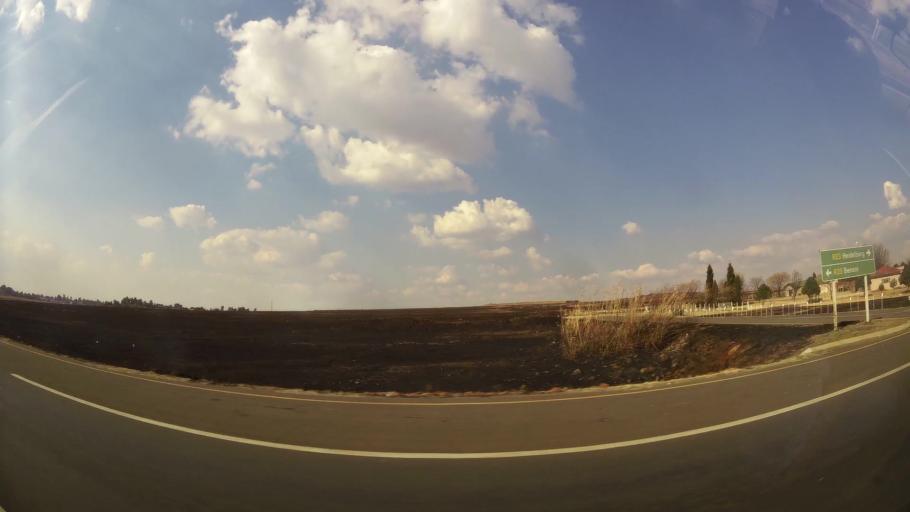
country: ZA
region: Gauteng
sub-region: Ekurhuleni Metropolitan Municipality
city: Brakpan
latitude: -26.3068
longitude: 28.3361
